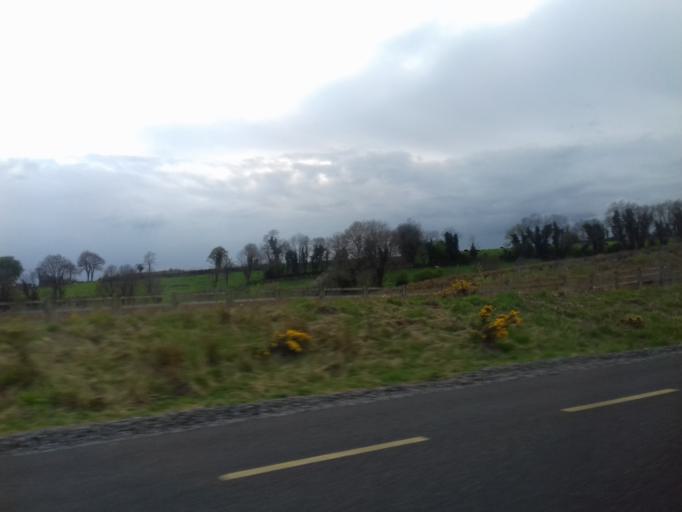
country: IE
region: Ulster
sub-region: An Cabhan
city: Belturbet
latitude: 54.0896
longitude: -7.4515
